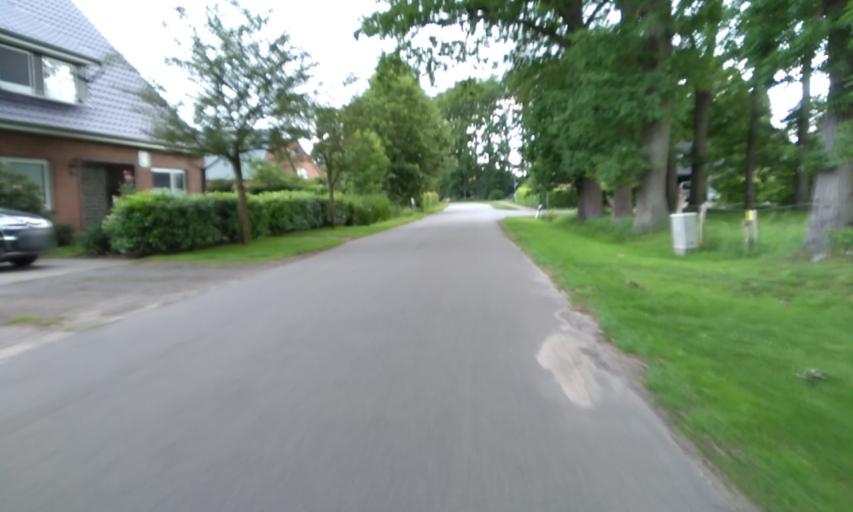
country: DE
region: Lower Saxony
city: Sauensiek
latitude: 53.3815
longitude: 9.6046
